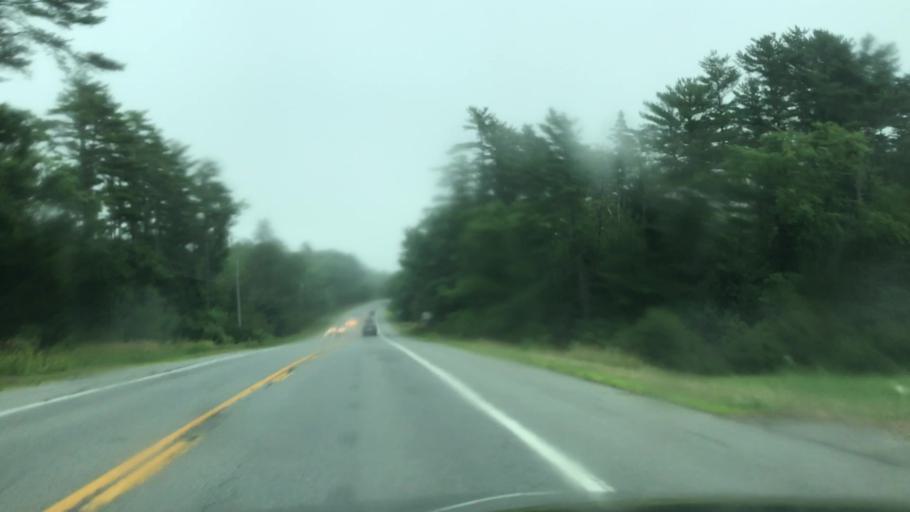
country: US
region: Maine
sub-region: Lincoln County
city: Nobleboro
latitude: 44.1034
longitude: -69.4404
